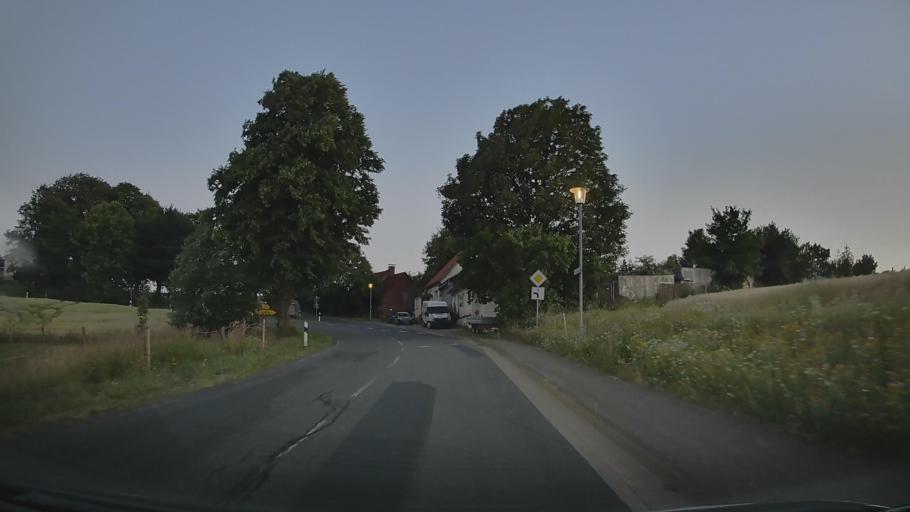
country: DE
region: North Rhine-Westphalia
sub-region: Regierungsbezirk Detmold
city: Lugde
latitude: 51.9571
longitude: 9.2986
